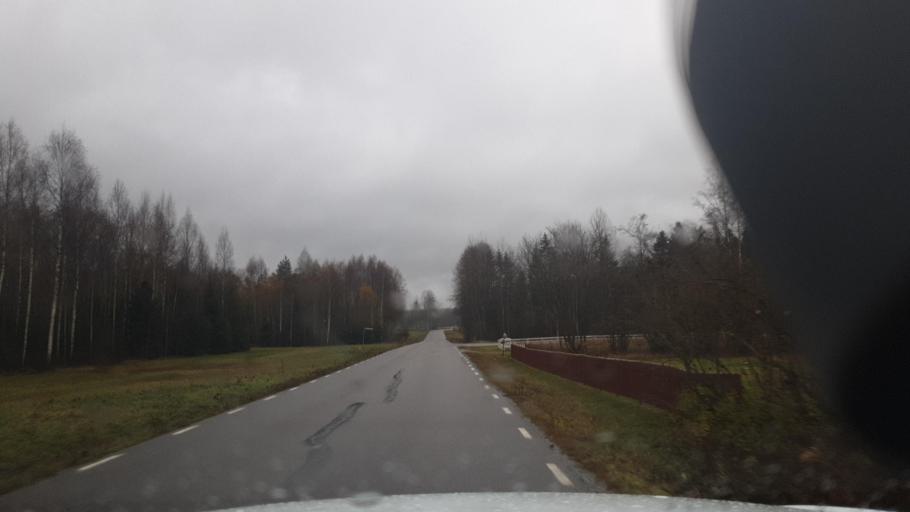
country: SE
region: Vaermland
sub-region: Eda Kommun
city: Amotfors
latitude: 59.7207
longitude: 12.1609
